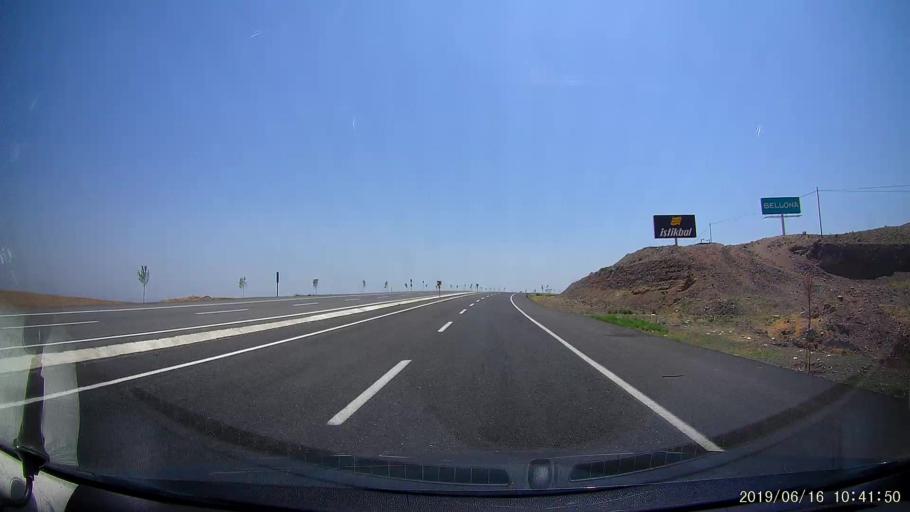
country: AM
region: Armavir
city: Shenavan
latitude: 40.0455
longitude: 43.7931
